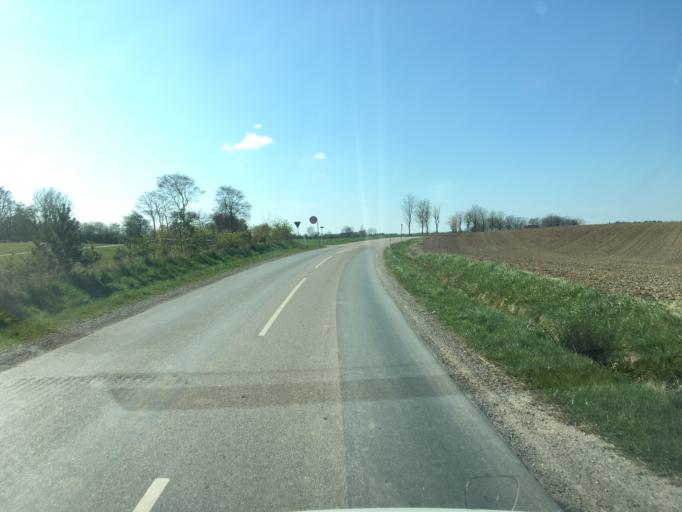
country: DK
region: South Denmark
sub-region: Sonderborg Kommune
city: Grasten
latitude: 54.9035
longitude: 9.5537
